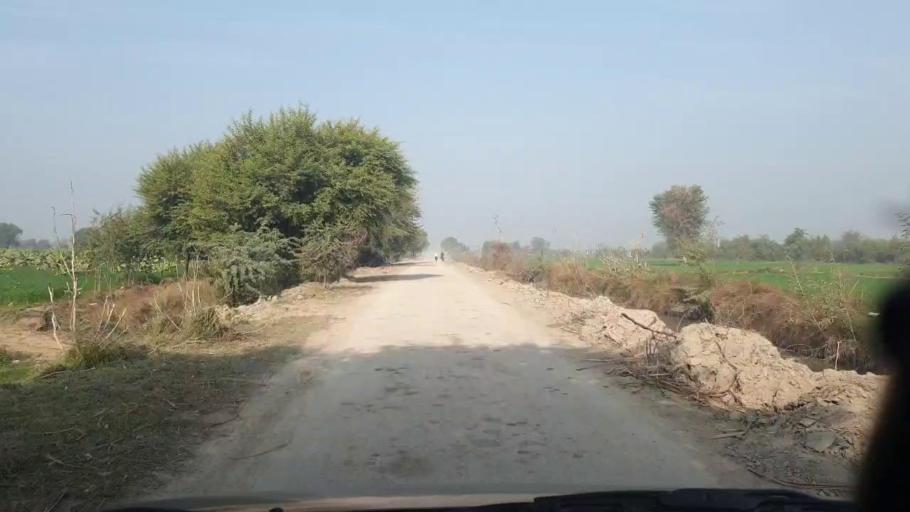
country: PK
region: Sindh
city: Shahdadpur
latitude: 26.0324
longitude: 68.5414
